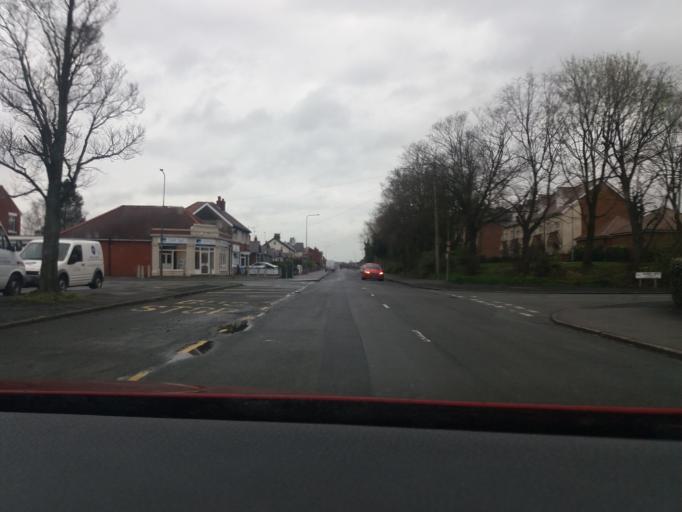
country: GB
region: England
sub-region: Lancashire
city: Chorley
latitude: 53.6427
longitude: -2.6293
